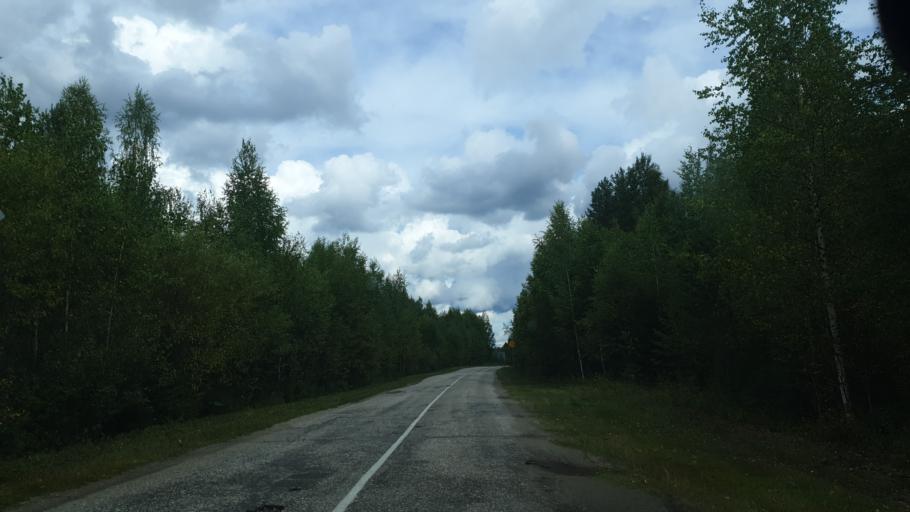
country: RU
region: Komi Republic
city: Aykino
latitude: 61.9352
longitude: 50.1555
